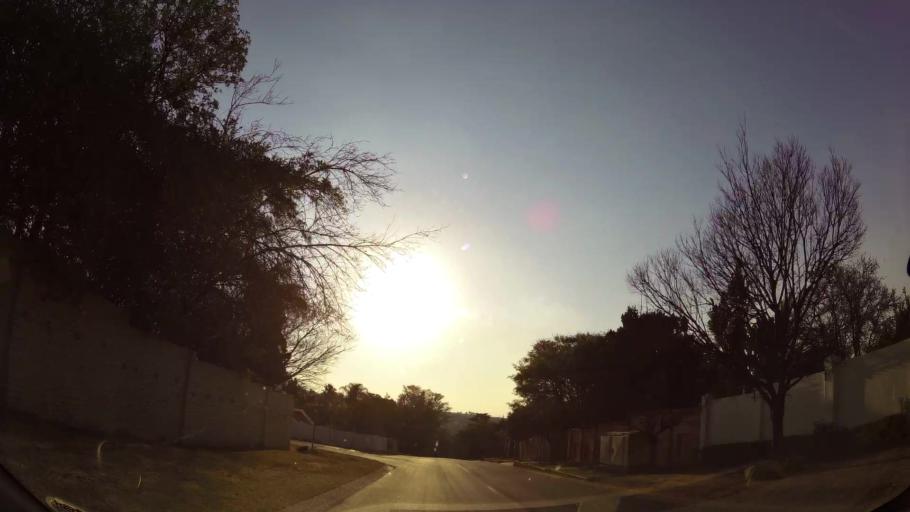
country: ZA
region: Gauteng
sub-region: City of Johannesburg Metropolitan Municipality
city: Diepsloot
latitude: -26.0613
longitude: 27.9869
